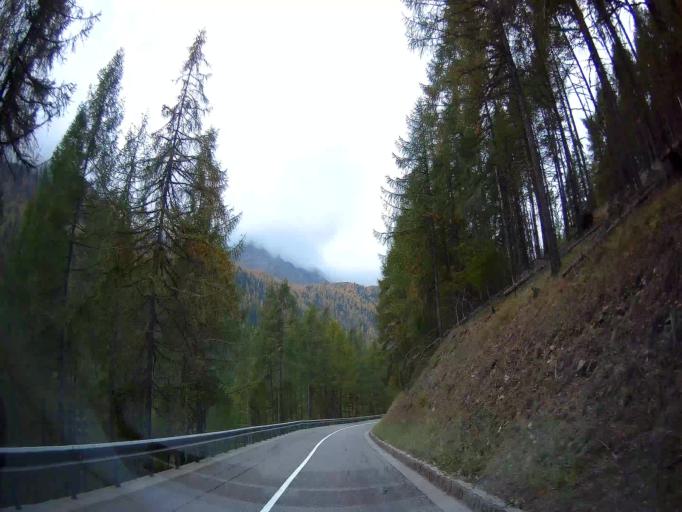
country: IT
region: Trentino-Alto Adige
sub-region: Bolzano
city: Senales
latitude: 46.7370
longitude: 10.8226
